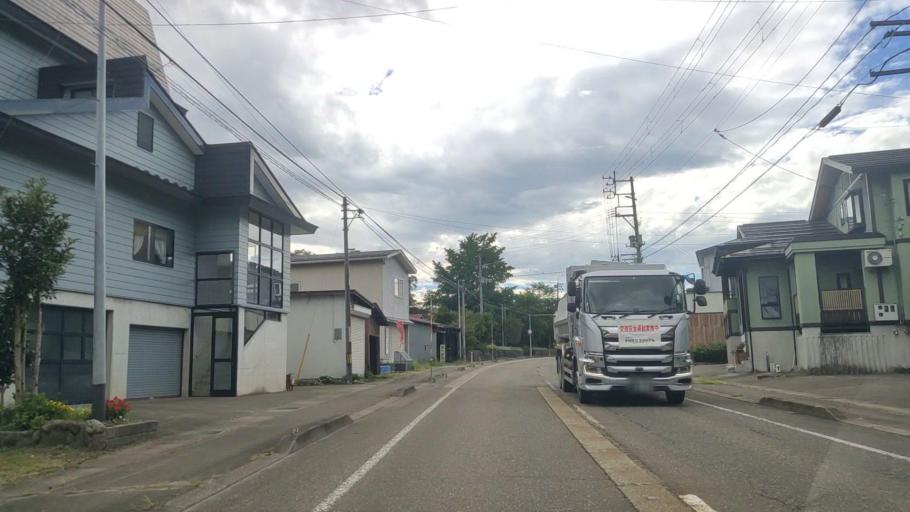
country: JP
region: Niigata
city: Arai
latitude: 36.9861
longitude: 138.2721
